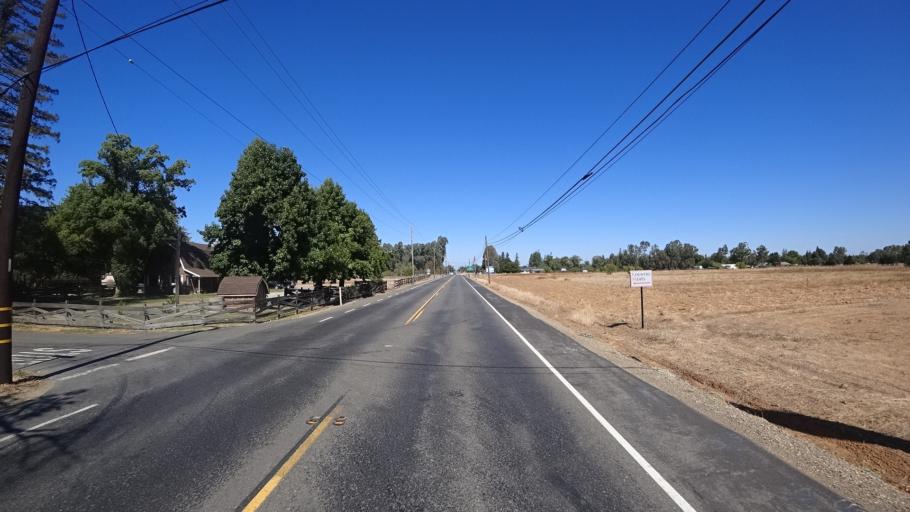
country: US
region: California
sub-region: Sacramento County
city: Vineyard
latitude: 38.4345
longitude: -121.3347
